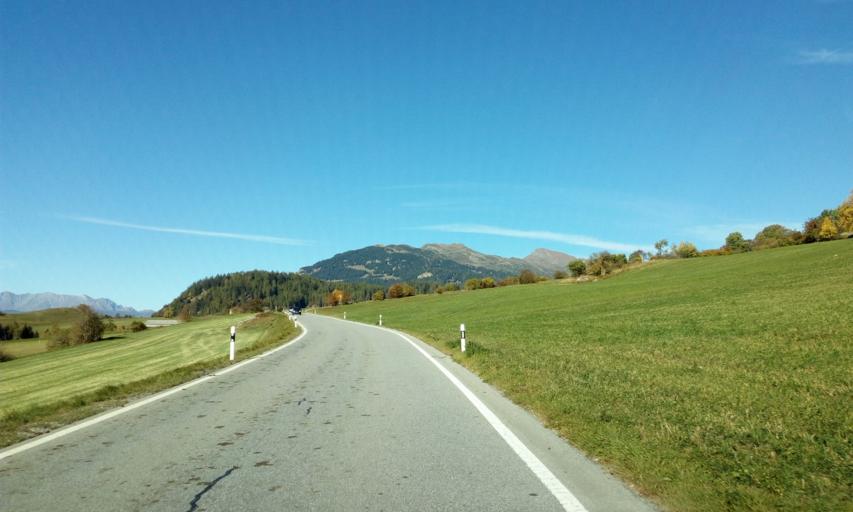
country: CH
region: Grisons
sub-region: Albula District
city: Tiefencastel
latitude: 46.6769
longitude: 9.5748
